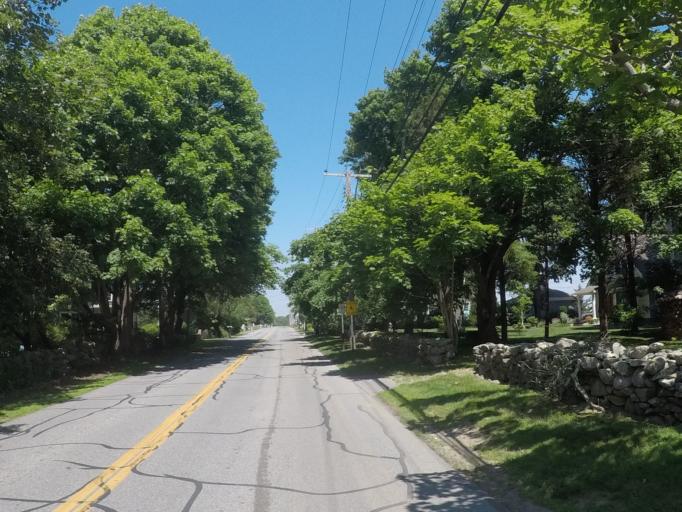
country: US
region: Massachusetts
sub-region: Bristol County
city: Bliss Corner
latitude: 41.5405
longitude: -70.9527
